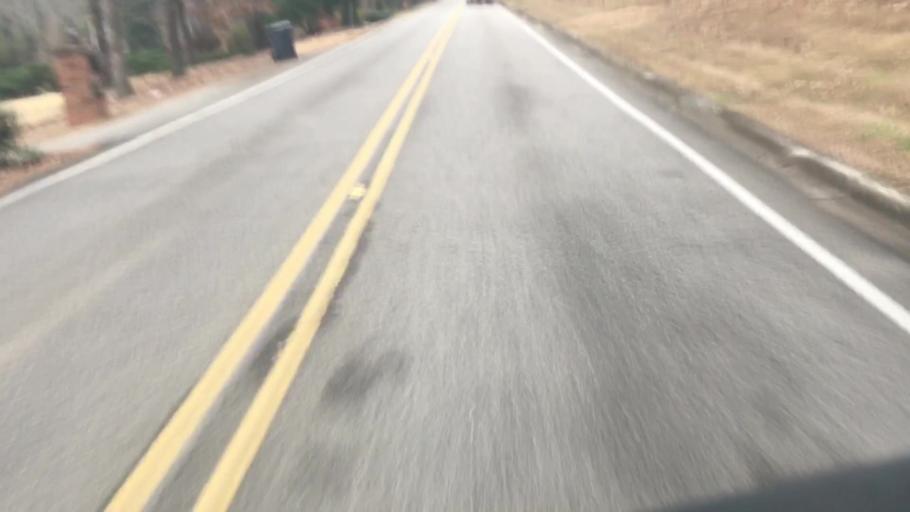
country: US
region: Alabama
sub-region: Jefferson County
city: Vestavia Hills
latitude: 33.4164
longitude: -86.7634
